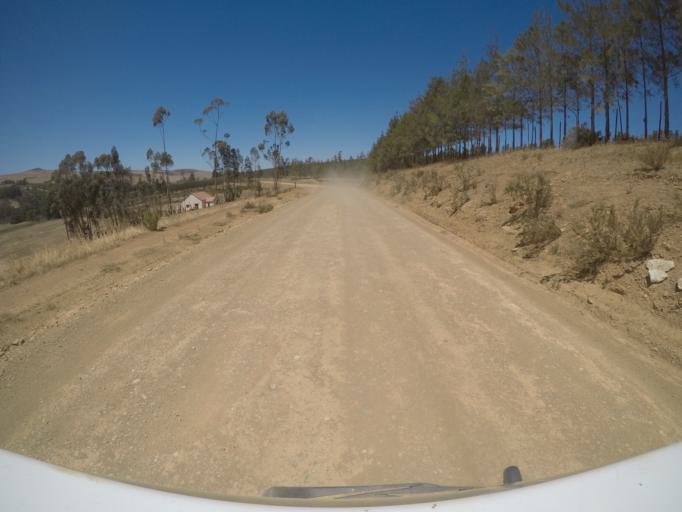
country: ZA
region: Western Cape
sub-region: Overberg District Municipality
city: Grabouw
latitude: -34.0904
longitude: 19.1916
